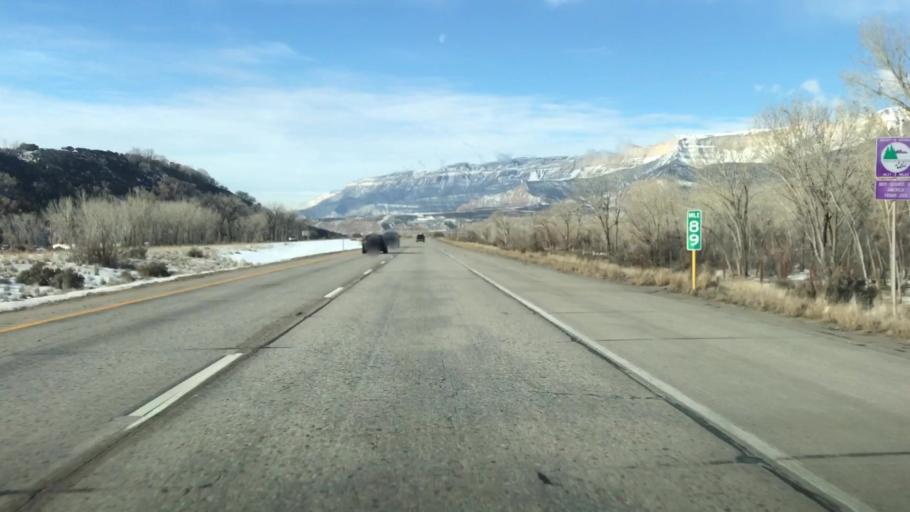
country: US
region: Colorado
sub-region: Garfield County
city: Rifle
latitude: 39.5203
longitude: -107.8036
